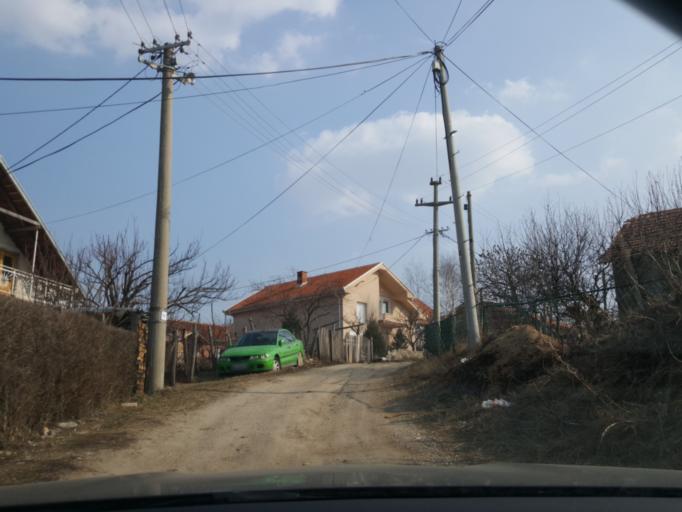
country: RS
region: Central Serbia
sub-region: Nisavski Okrug
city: Aleksinac
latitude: 43.5371
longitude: 21.7210
